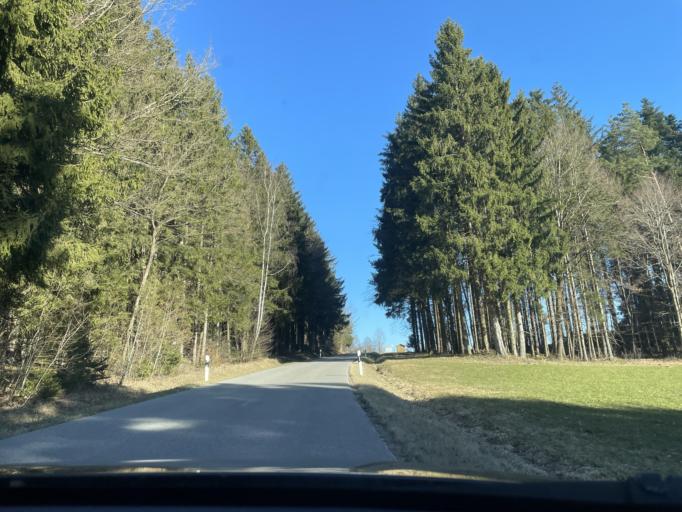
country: DE
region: Bavaria
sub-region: Lower Bavaria
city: Geiersthal
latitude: 49.0808
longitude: 12.9622
